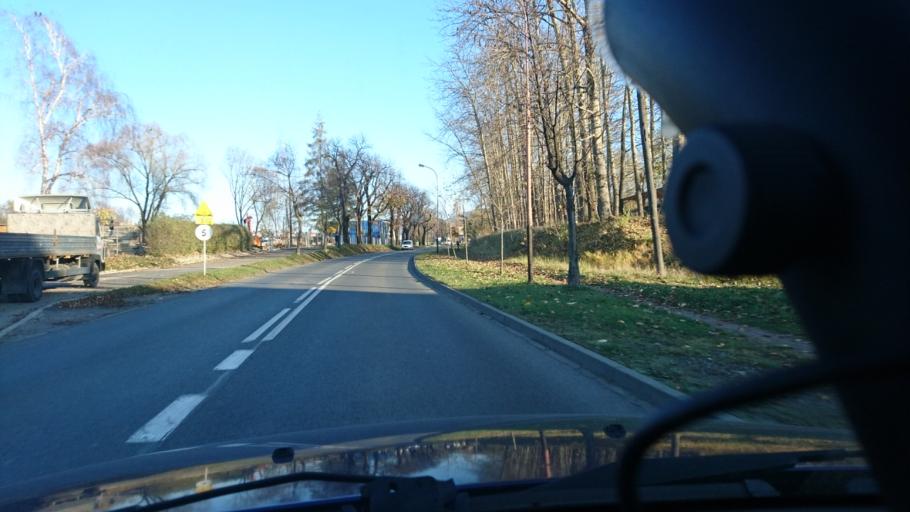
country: PL
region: Silesian Voivodeship
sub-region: Bielsko-Biala
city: Bielsko-Biala
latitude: 49.8341
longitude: 19.0594
